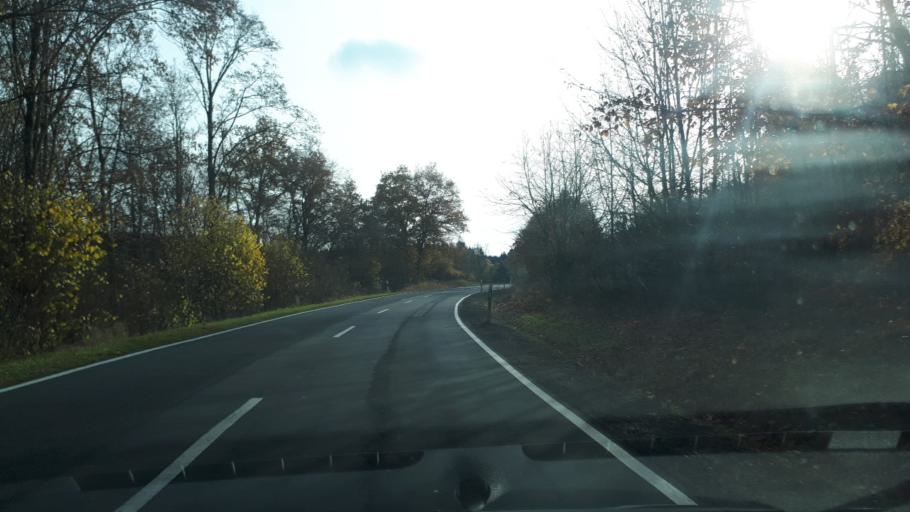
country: DE
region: Rheinland-Pfalz
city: Mullenbach
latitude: 50.1903
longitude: 7.0645
